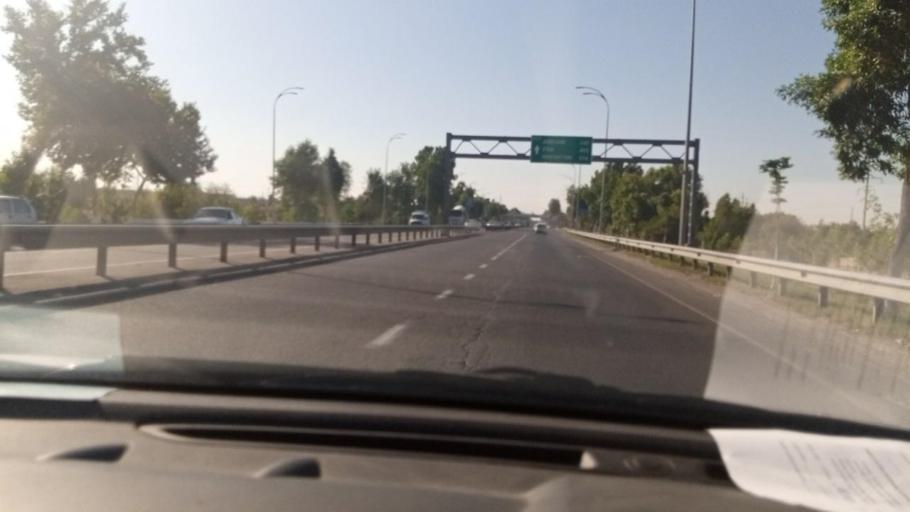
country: UZ
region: Toshkent Shahri
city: Bektemir
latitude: 41.2511
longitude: 69.3878
